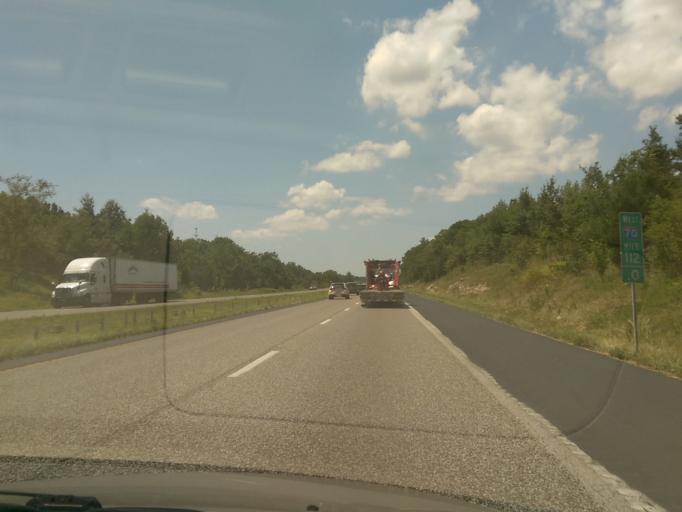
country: US
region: Missouri
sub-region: Cooper County
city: Boonville
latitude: 38.9401
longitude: -92.5841
